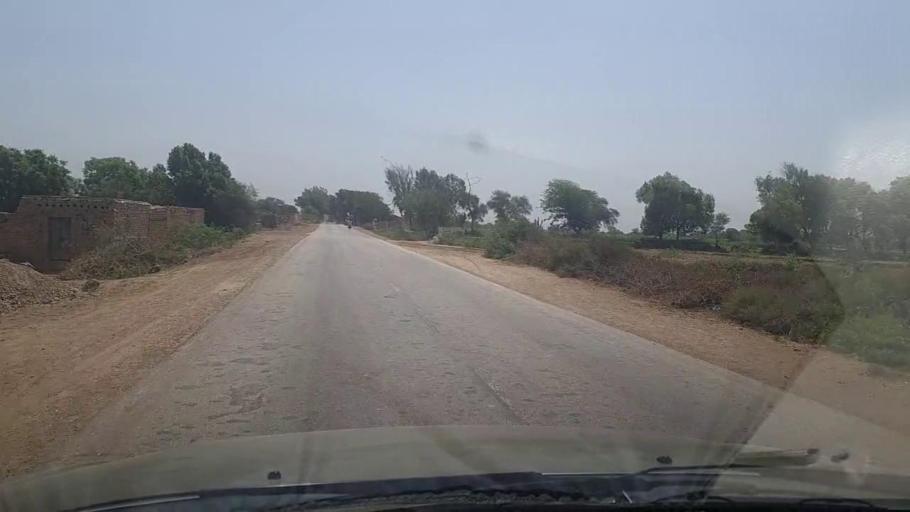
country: PK
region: Sindh
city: Hyderabad
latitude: 25.3780
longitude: 68.4574
